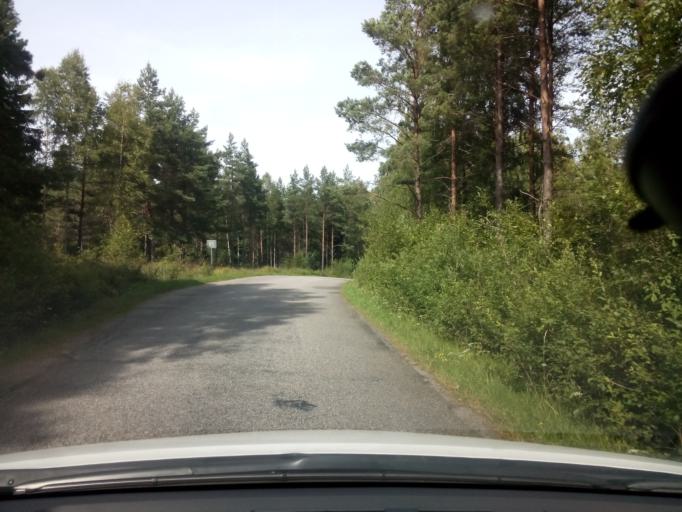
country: SE
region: Soedermanland
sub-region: Trosa Kommun
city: Trosa
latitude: 58.7613
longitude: 17.3695
